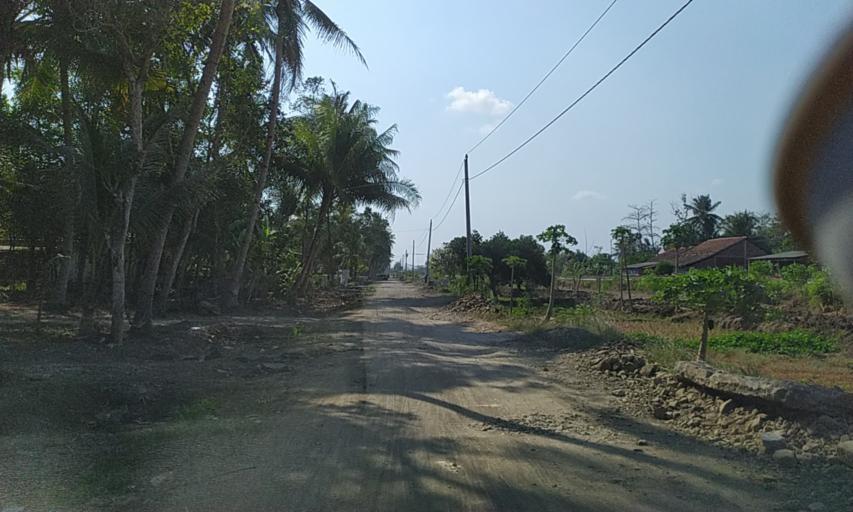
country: ID
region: Central Java
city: Alurbulu
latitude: -7.5061
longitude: 108.8349
